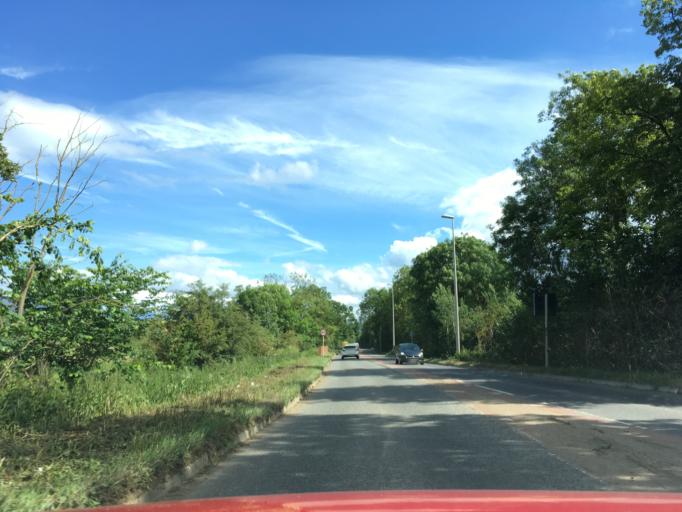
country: GB
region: England
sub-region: Milton Keynes
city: Broughton
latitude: 52.0422
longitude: -0.6794
